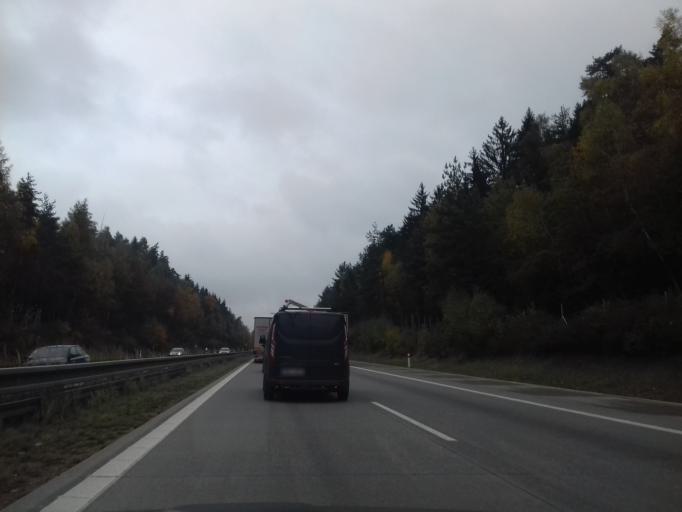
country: CZ
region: Central Bohemia
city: Cechtice
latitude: 49.6280
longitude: 15.1309
